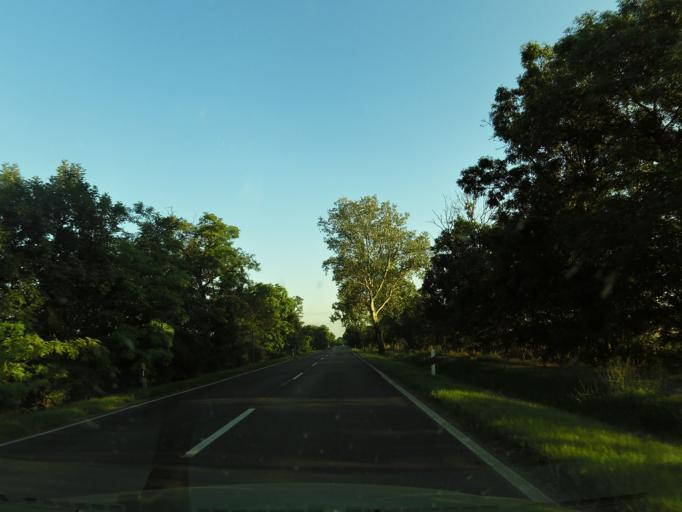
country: HU
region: Csongrad
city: Hodmezovasarhely
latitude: 46.4673
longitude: 20.3126
